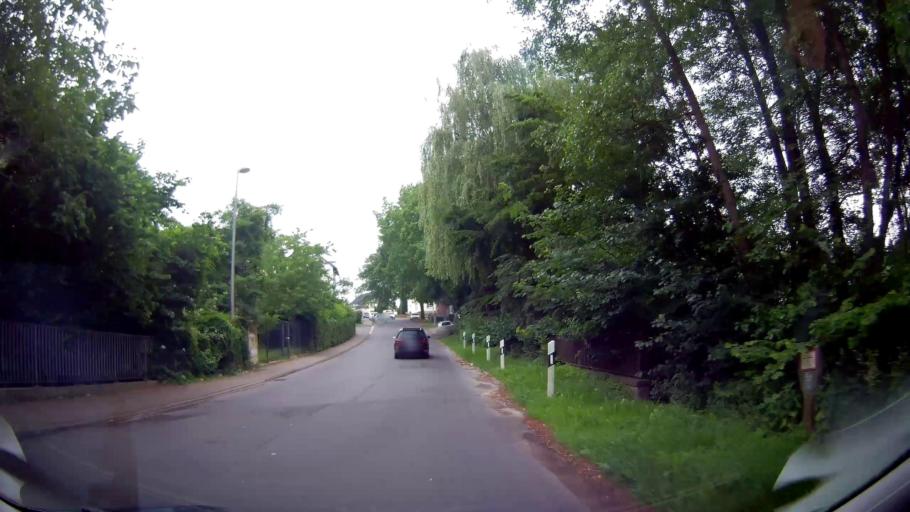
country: DE
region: North Rhine-Westphalia
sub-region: Regierungsbezirk Detmold
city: Herford
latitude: 52.1298
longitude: 8.7036
